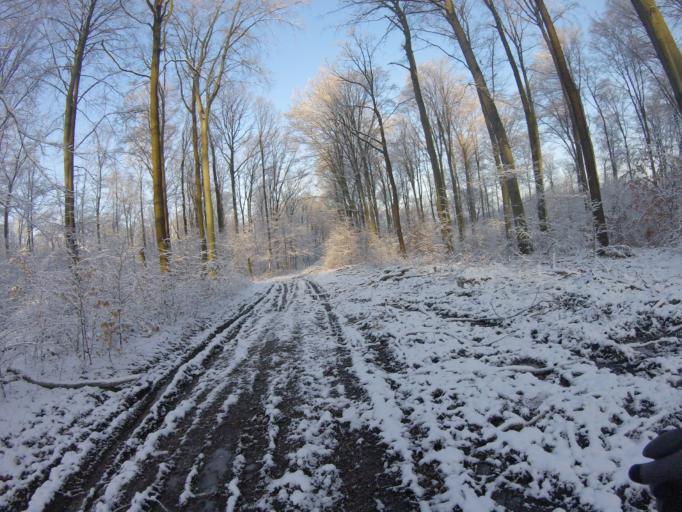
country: HU
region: Pest
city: Pilisszentkereszt
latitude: 47.7228
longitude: 18.8616
